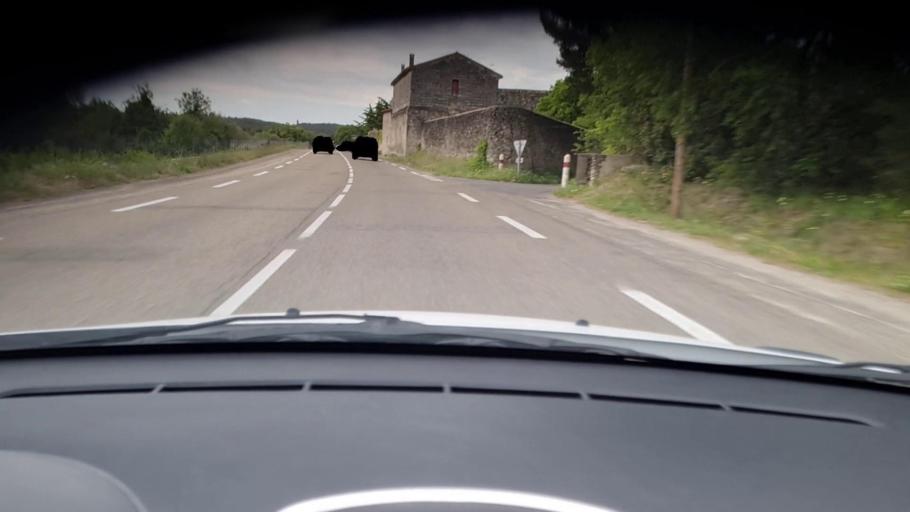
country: FR
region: Languedoc-Roussillon
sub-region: Departement du Gard
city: Uzes
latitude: 43.9964
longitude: 4.4132
